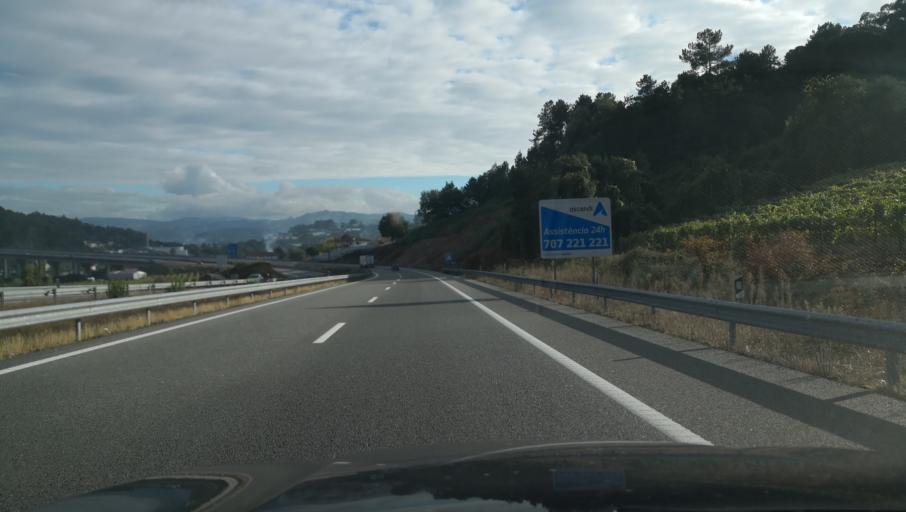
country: PT
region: Braga
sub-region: Guimaraes
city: Candoso
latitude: 41.4152
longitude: -8.3247
